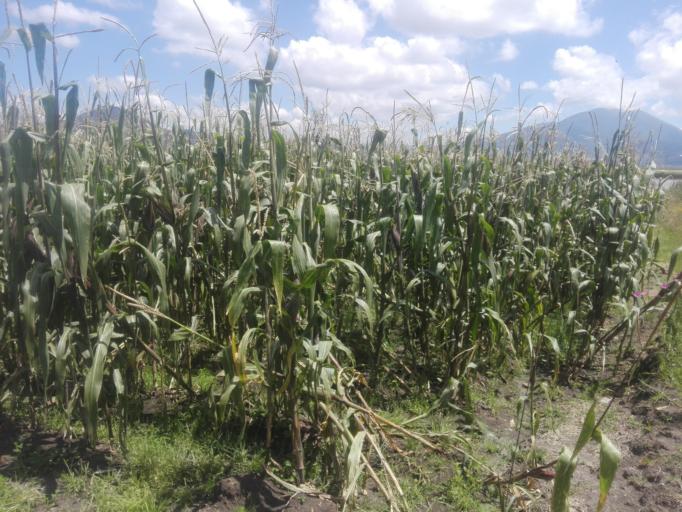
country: MX
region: Mexico
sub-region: Jocotitlan
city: Concepcion Caro
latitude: 19.7625
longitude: -99.9015
